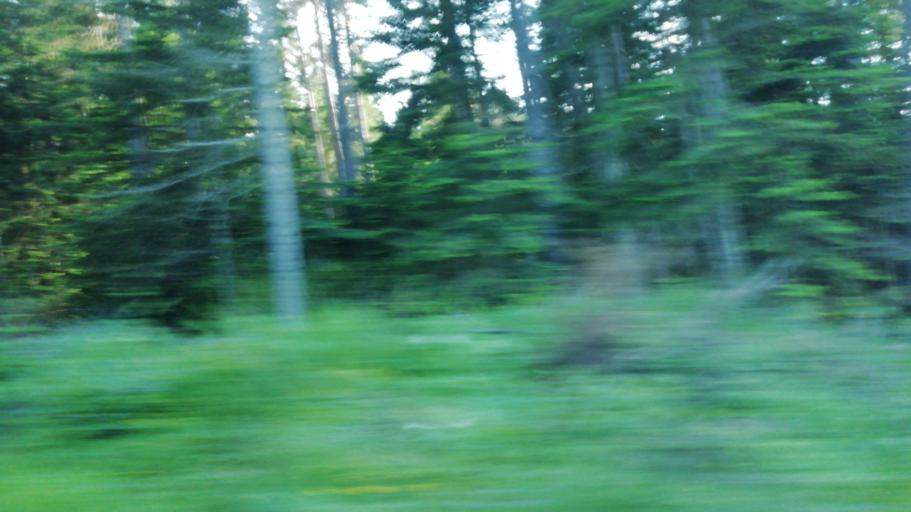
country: TR
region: Karabuk
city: Eskipazar
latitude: 41.0488
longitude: 32.5434
